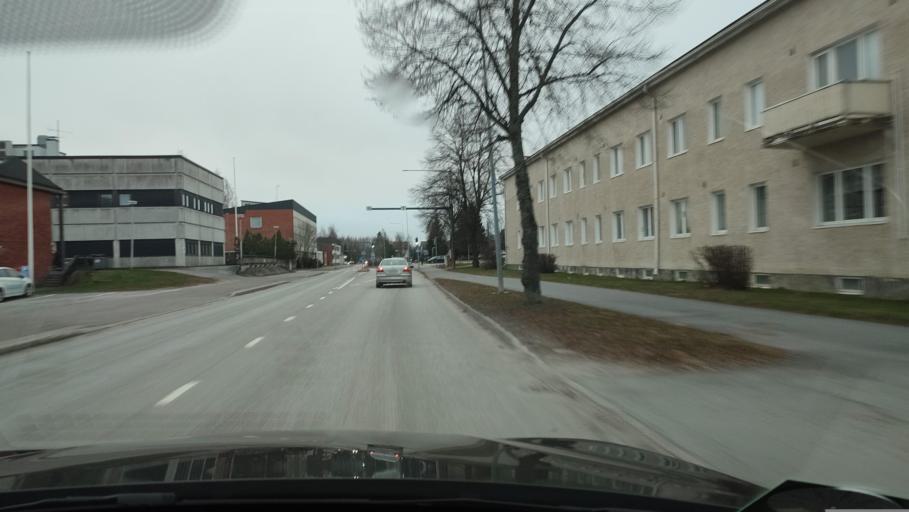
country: FI
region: Southern Ostrobothnia
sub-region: Suupohja
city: Kauhajoki
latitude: 62.4244
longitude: 22.1763
